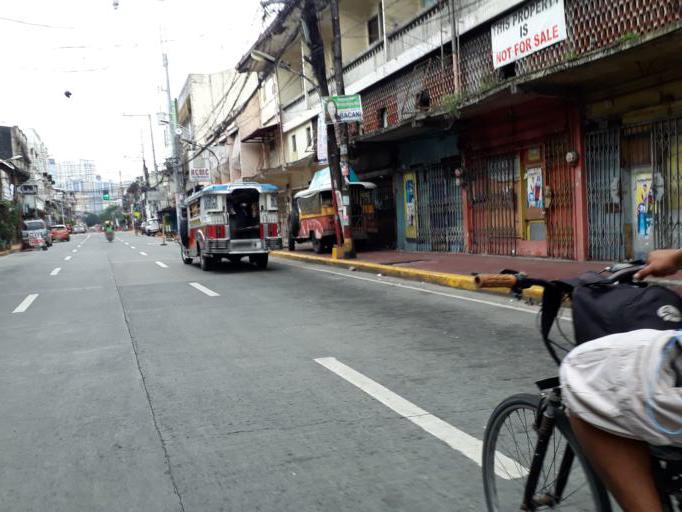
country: PH
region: Metro Manila
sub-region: City of Manila
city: Manila
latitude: 14.6115
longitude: 120.9942
